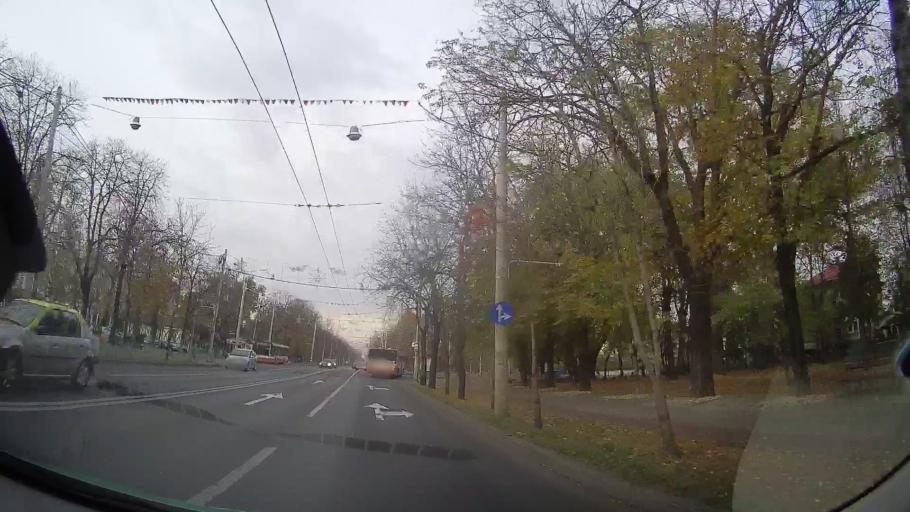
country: RO
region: Prahova
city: Ploiesti
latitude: 44.9297
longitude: 26.0283
